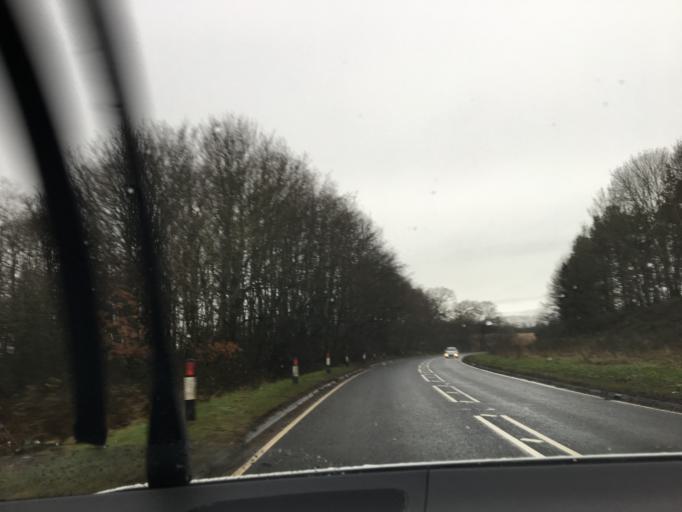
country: GB
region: Scotland
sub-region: Stirling
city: Doune
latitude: 56.1685
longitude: -4.0668
